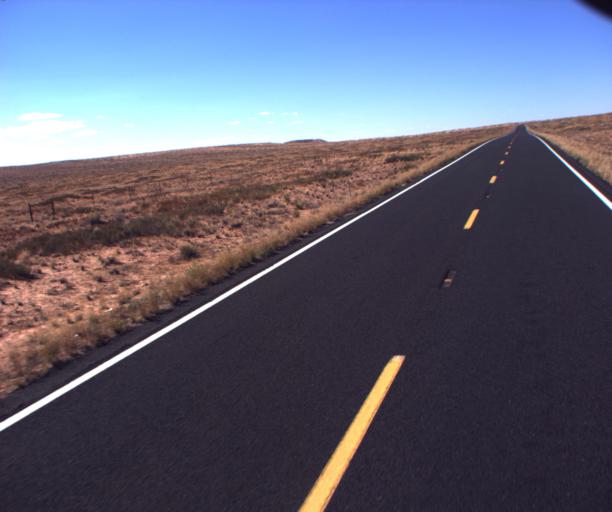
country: US
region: Arizona
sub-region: Coconino County
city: Tuba City
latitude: 36.0335
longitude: -111.1747
